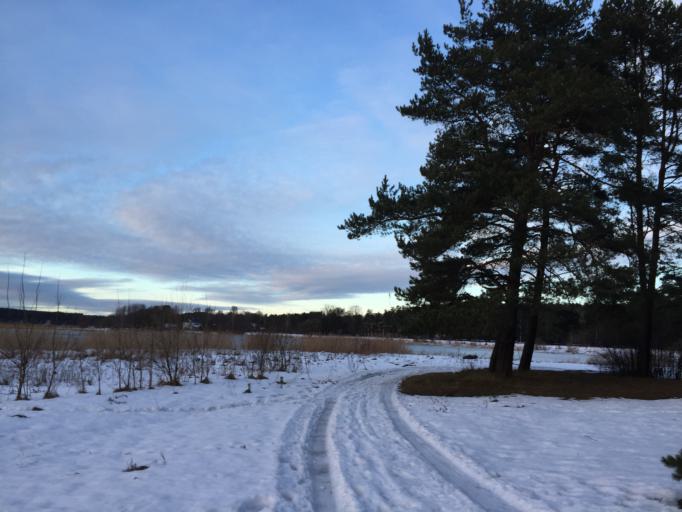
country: LV
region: Riga
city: Bergi
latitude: 56.9744
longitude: 24.3048
